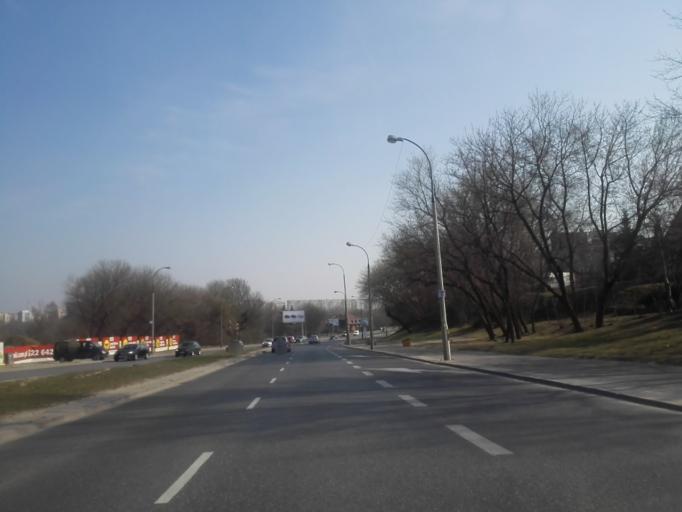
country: PL
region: Masovian Voivodeship
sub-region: Warszawa
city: Mokotow
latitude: 52.1770
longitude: 21.0350
